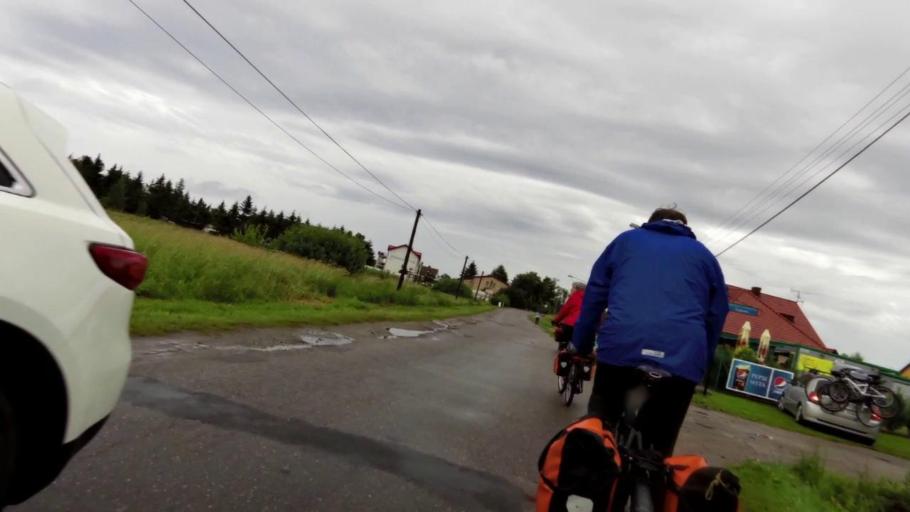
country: PL
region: West Pomeranian Voivodeship
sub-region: Powiat kolobrzeski
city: Ustronie Morskie
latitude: 54.2424
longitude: 15.8867
